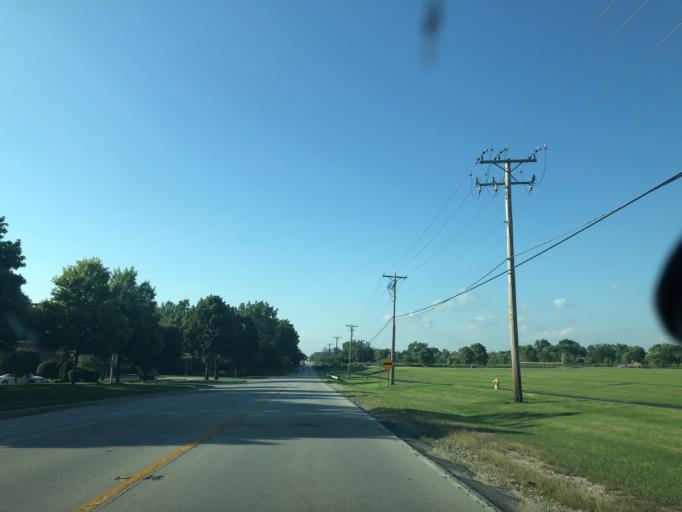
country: US
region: Illinois
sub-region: Will County
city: Mokena
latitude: 41.5678
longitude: -87.8905
